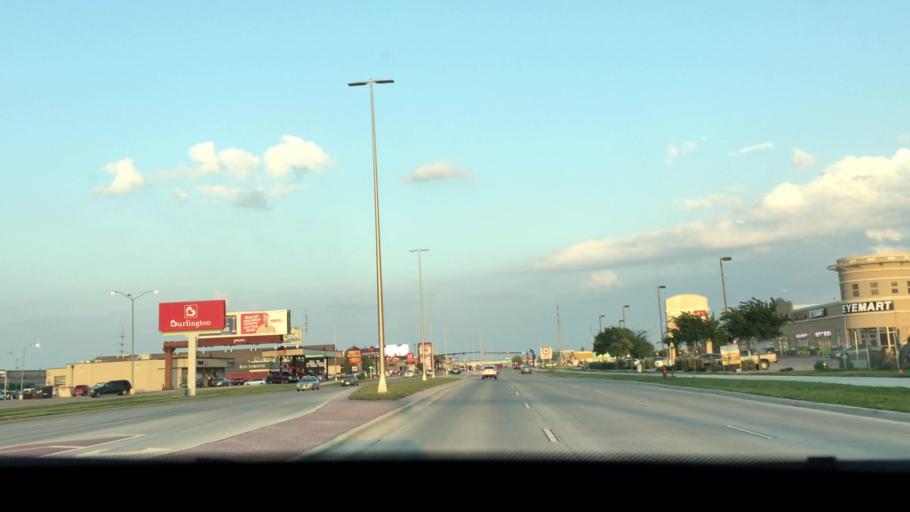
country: US
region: North Dakota
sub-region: Cass County
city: West Fargo
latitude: 46.8618
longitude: -96.8560
